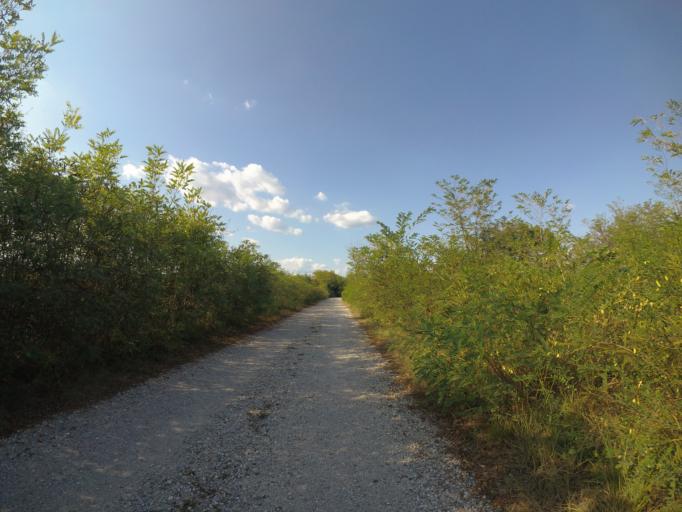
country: IT
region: Friuli Venezia Giulia
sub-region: Provincia di Udine
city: Basaldella
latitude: 46.0183
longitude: 13.1945
